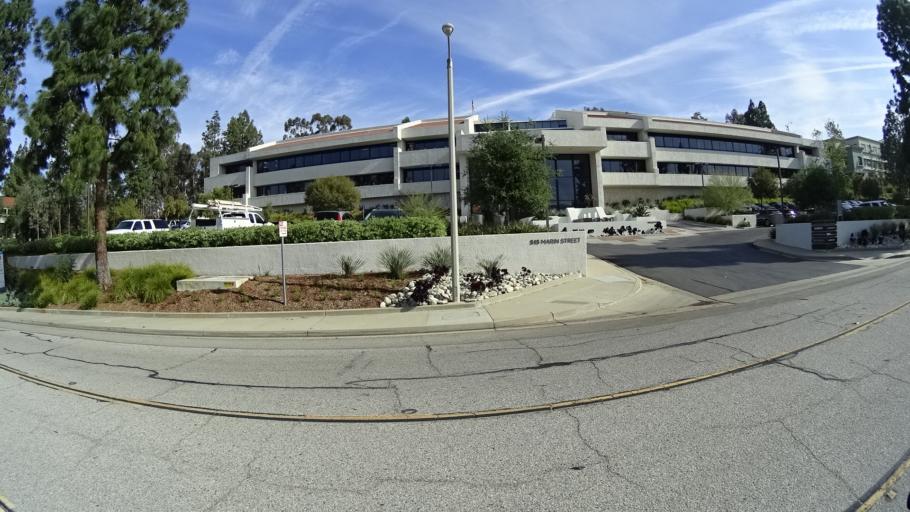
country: US
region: California
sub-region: Ventura County
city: Thousand Oaks
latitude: 34.1837
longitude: -118.8819
